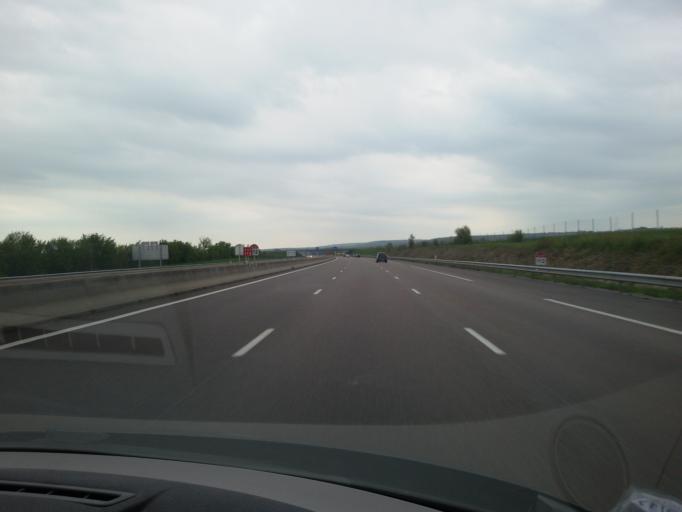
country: FR
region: Champagne-Ardenne
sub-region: Departement de la Haute-Marne
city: Rolampont
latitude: 47.8930
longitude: 5.2241
